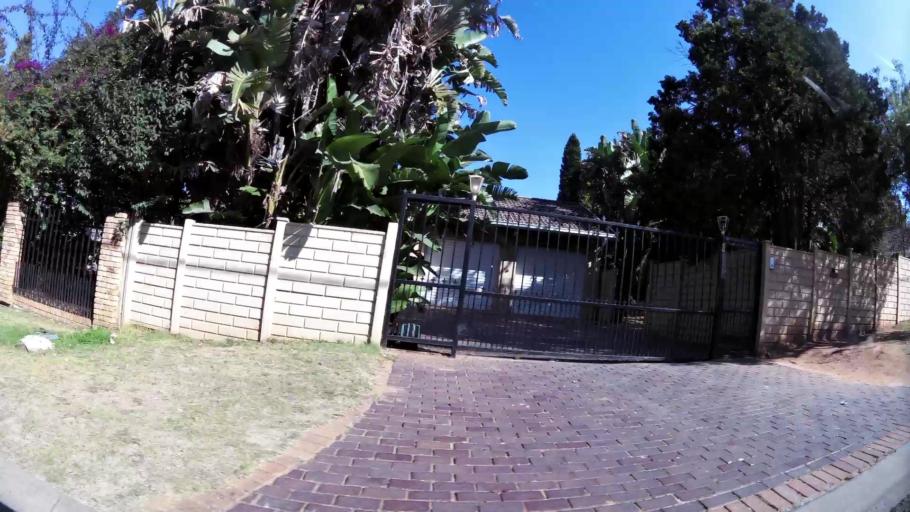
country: ZA
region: Gauteng
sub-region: City of Johannesburg Metropolitan Municipality
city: Modderfontein
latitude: -26.1198
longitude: 28.1070
